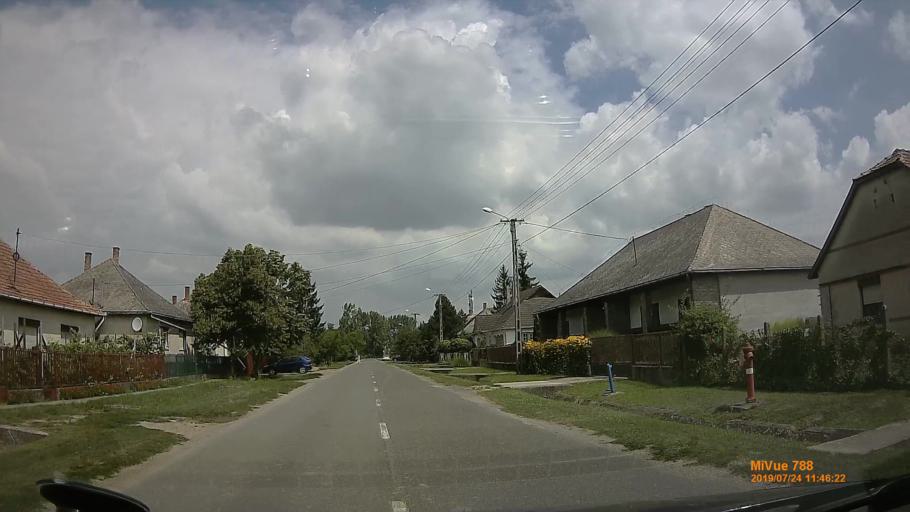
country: UA
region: Zakarpattia
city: Batiovo
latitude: 48.2378
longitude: 22.4351
